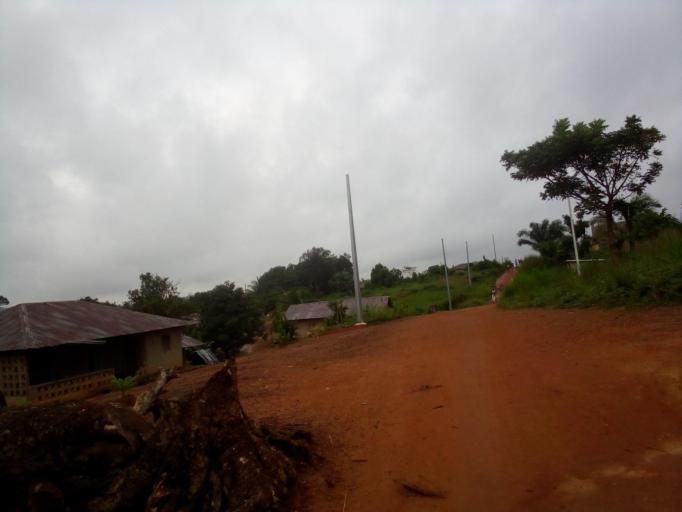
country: SL
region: Eastern Province
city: Kailahun
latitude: 8.2758
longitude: -10.5828
